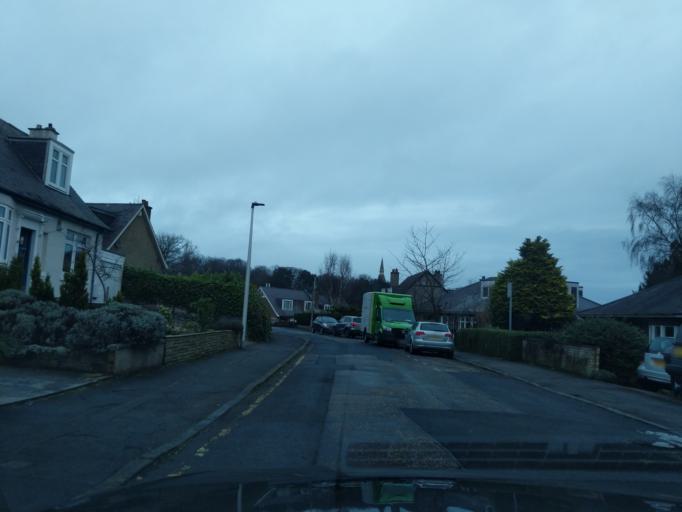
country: GB
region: Scotland
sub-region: Edinburgh
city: Edinburgh
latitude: 55.9600
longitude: -3.2323
